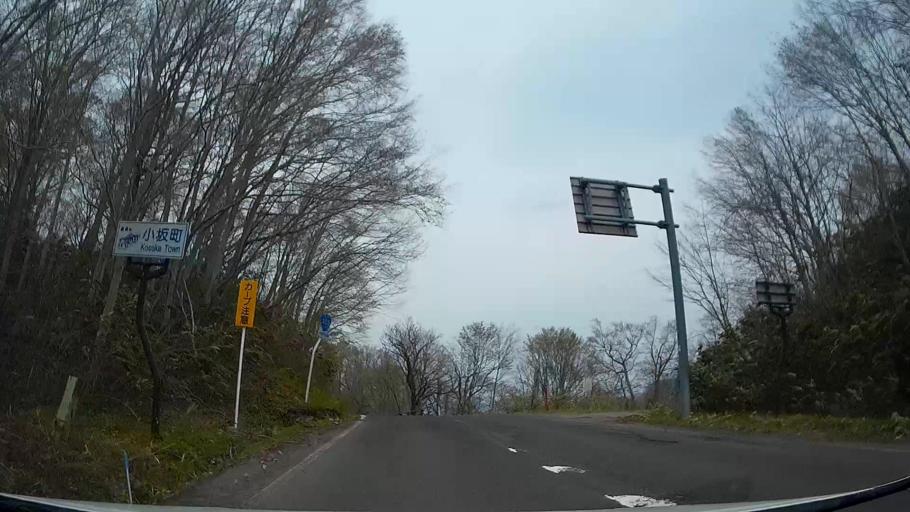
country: JP
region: Akita
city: Hanawa
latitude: 40.4064
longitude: 140.8653
